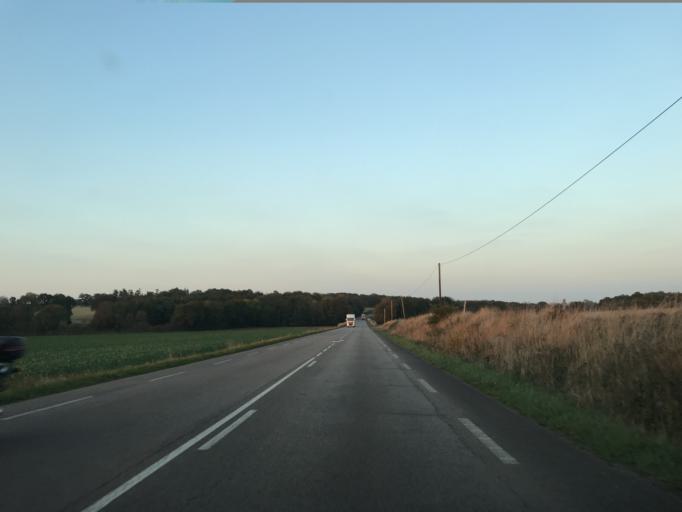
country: FR
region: Haute-Normandie
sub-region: Departement de l'Eure
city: Bourth
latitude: 48.6956
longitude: 0.8260
